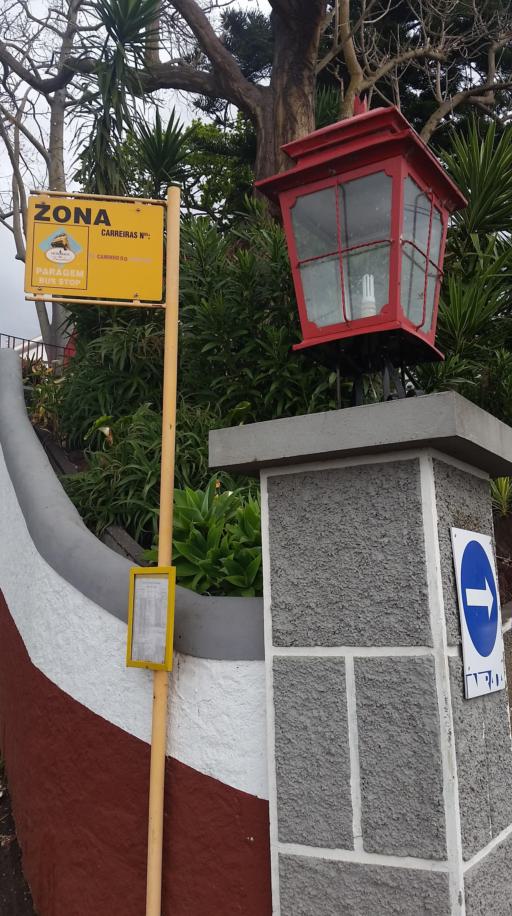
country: PT
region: Madeira
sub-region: Funchal
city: Nossa Senhora do Monte
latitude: 32.6766
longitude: -16.9464
